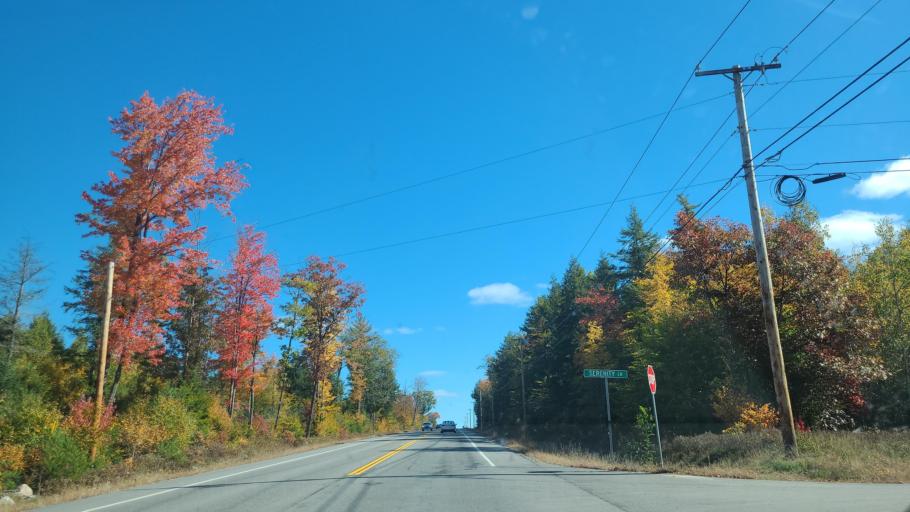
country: US
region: Maine
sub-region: Oxford County
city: Fryeburg
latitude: 44.0263
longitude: -70.9322
